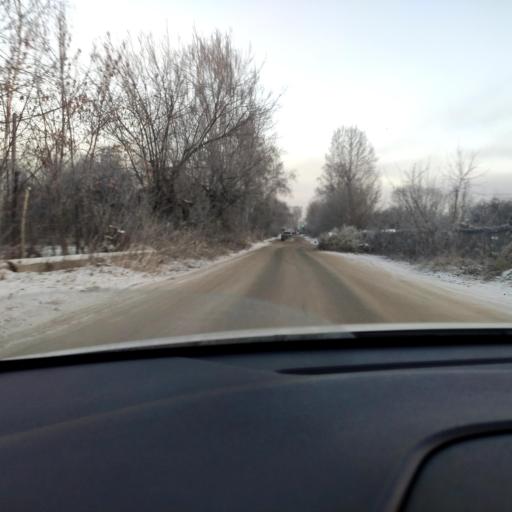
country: RU
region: Tatarstan
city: Staroye Arakchino
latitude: 55.8639
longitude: 49.0468
